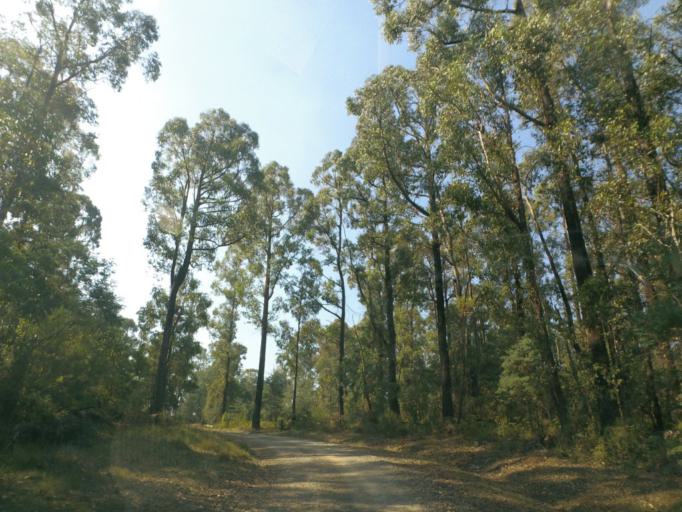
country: AU
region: Victoria
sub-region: Yarra Ranges
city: Millgrove
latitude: -37.5266
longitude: 145.7439
